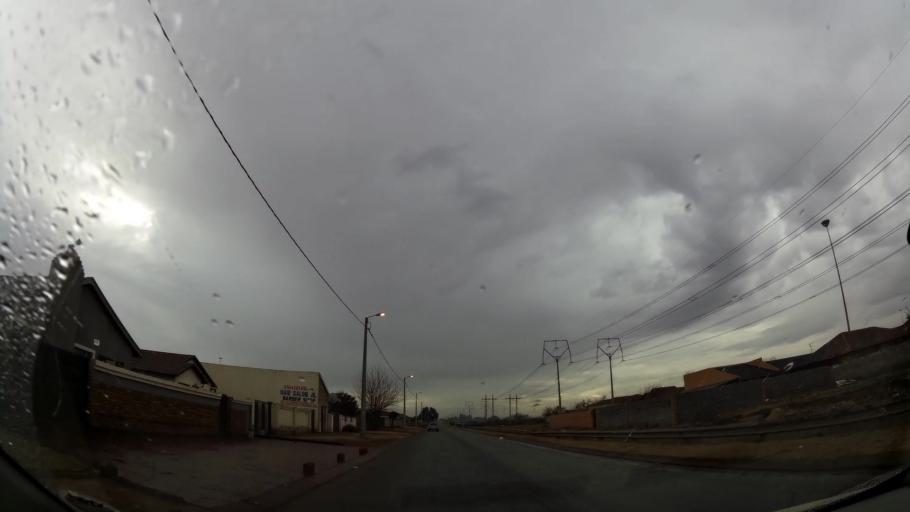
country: ZA
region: Gauteng
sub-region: Ekurhuleni Metropolitan Municipality
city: Germiston
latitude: -26.3371
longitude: 28.2037
